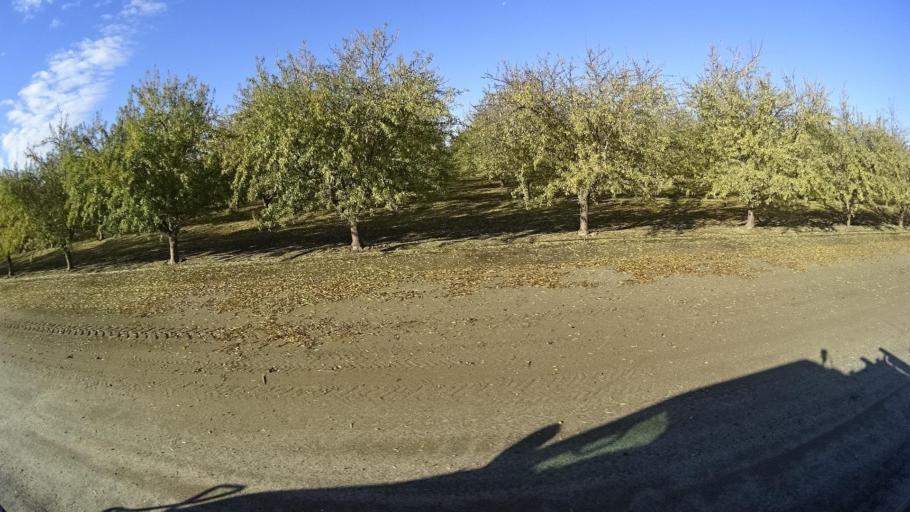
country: US
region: California
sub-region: Kern County
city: McFarland
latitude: 35.7079
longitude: -119.2942
